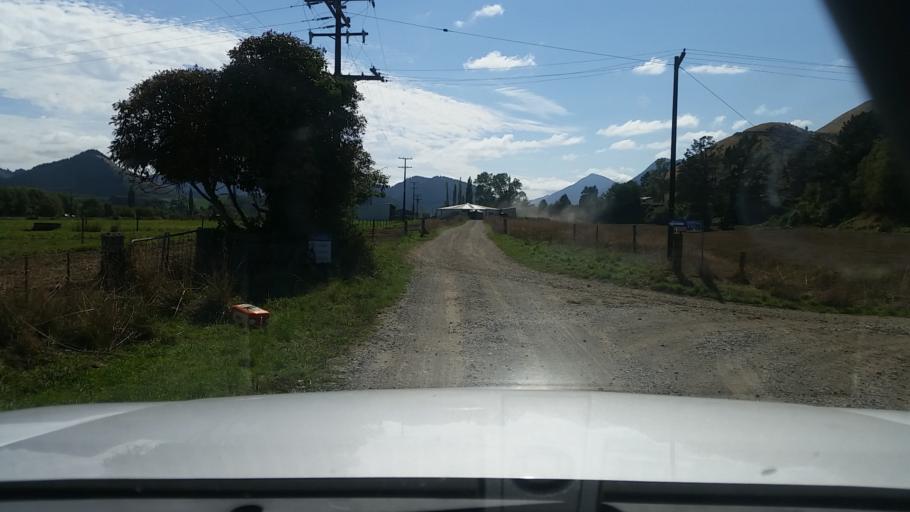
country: NZ
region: Nelson
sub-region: Nelson City
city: Nelson
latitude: -41.2504
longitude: 173.5831
